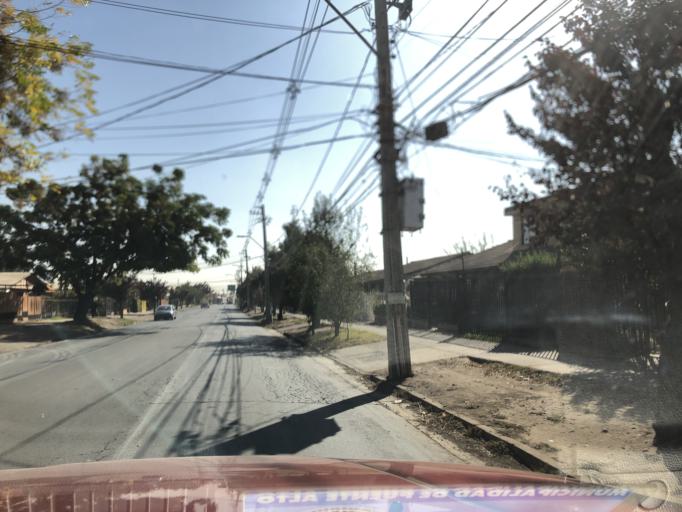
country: CL
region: Santiago Metropolitan
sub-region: Provincia de Cordillera
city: Puente Alto
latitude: -33.5744
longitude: -70.5710
